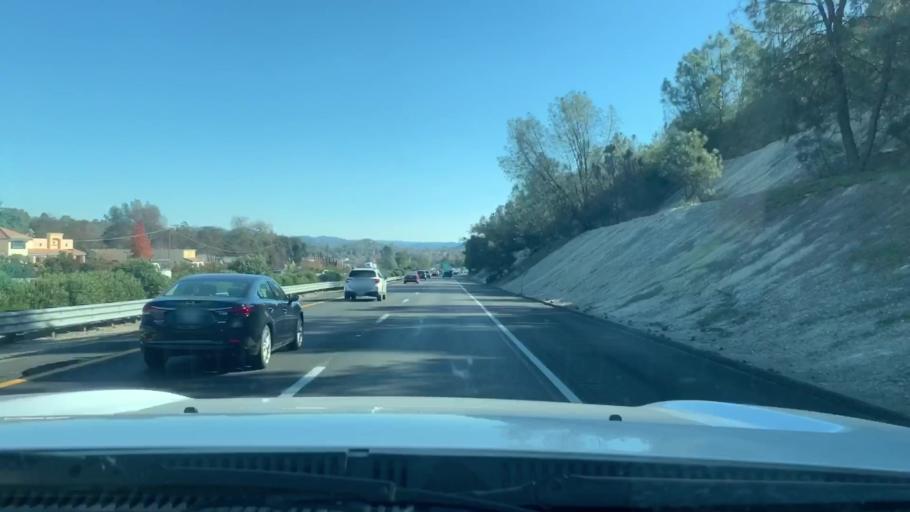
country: US
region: California
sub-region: San Luis Obispo County
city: Atascadero
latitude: 35.4932
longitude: -120.6777
